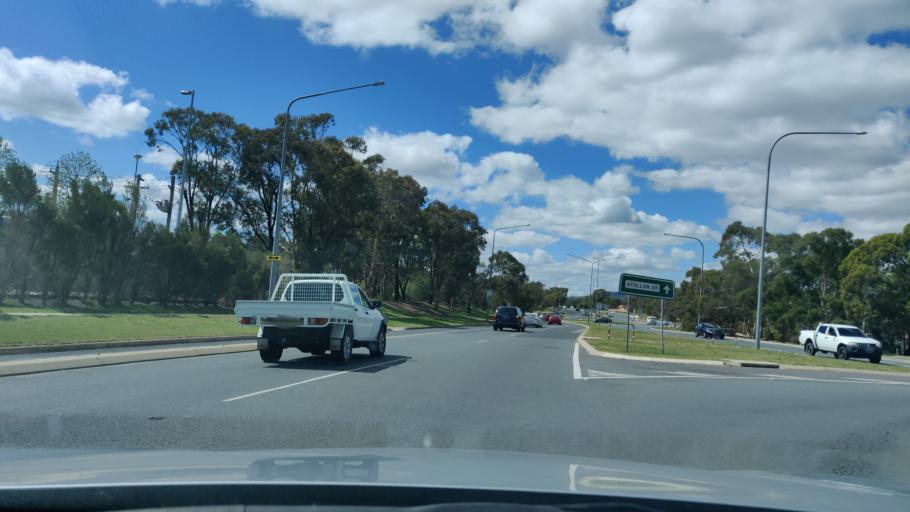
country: AU
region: Australian Capital Territory
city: Macarthur
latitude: -35.4249
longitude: 149.0725
